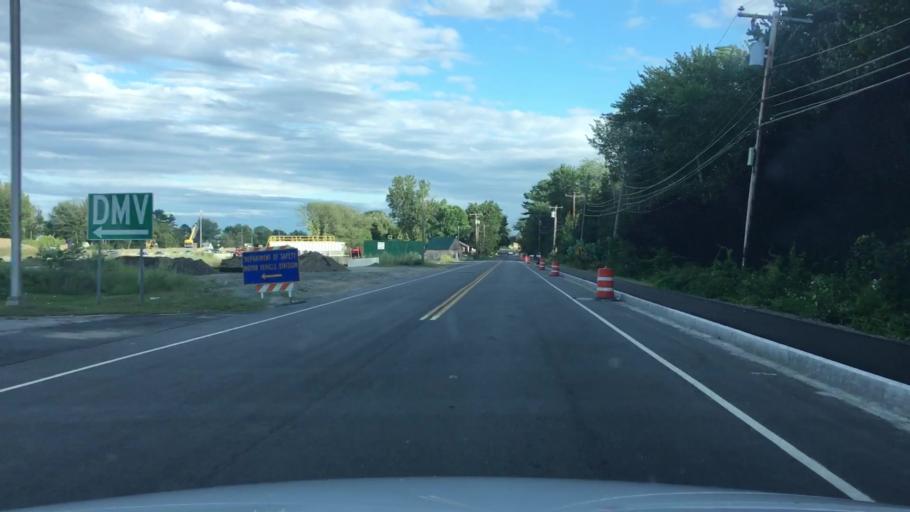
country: US
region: Maine
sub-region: York County
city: Eliot
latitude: 43.1252
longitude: -70.8367
